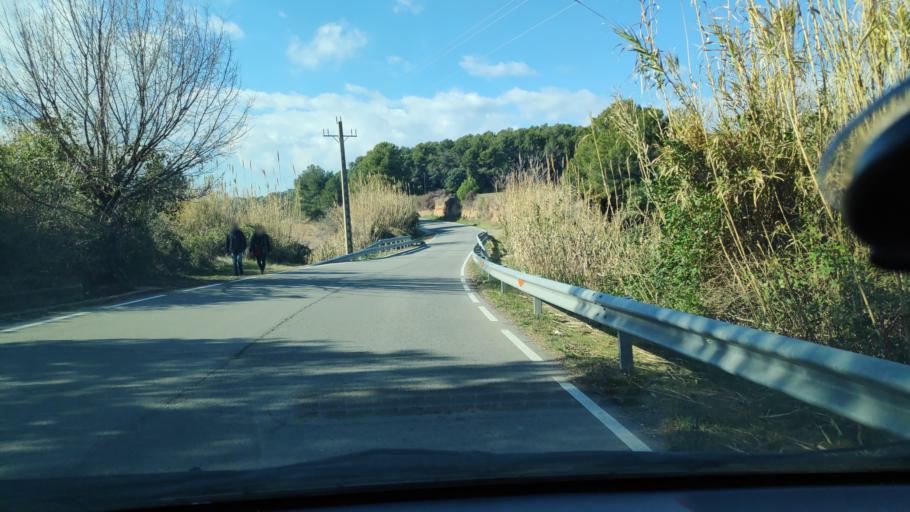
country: ES
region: Catalonia
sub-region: Provincia de Barcelona
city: Matadepera
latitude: 41.5963
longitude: 2.0167
